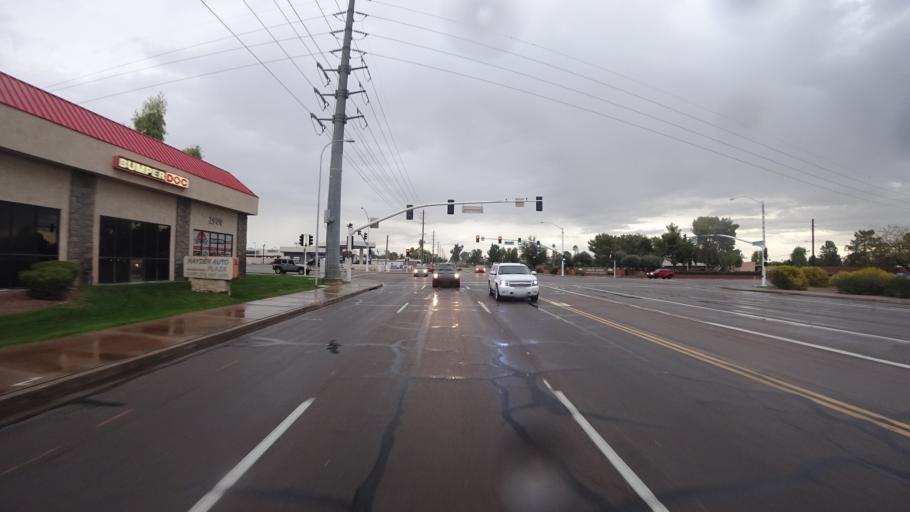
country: US
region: Arizona
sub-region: Maricopa County
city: Tempe
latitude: 33.4509
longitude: -111.9094
